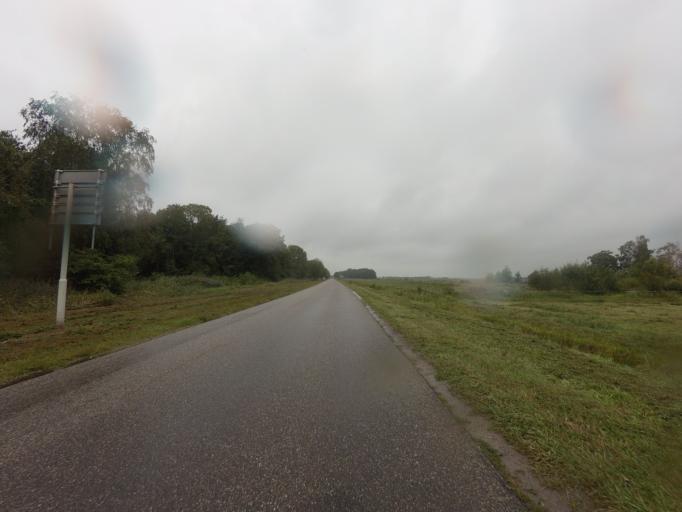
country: NL
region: Friesland
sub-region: Gemeente Tytsjerksteradiel
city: Garyp
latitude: 53.1317
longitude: 5.9587
